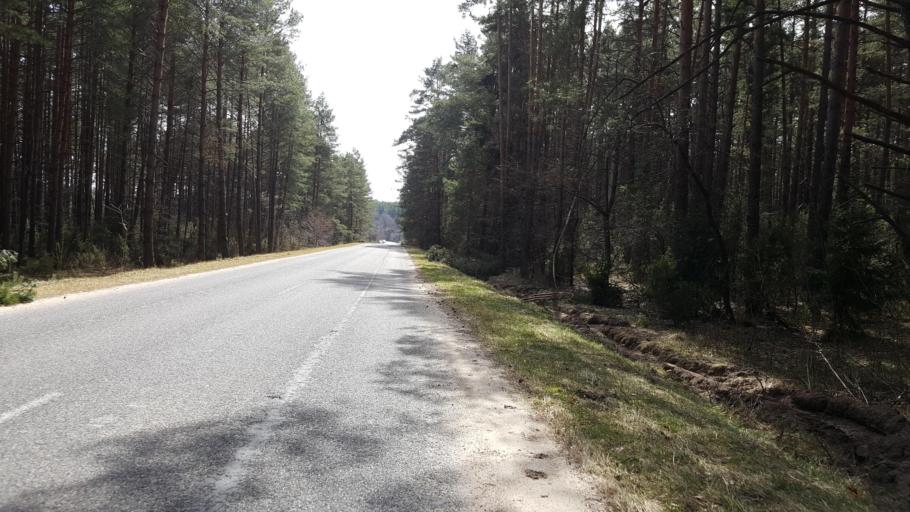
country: BY
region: Brest
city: Kamyanyuki
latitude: 52.5141
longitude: 23.8525
